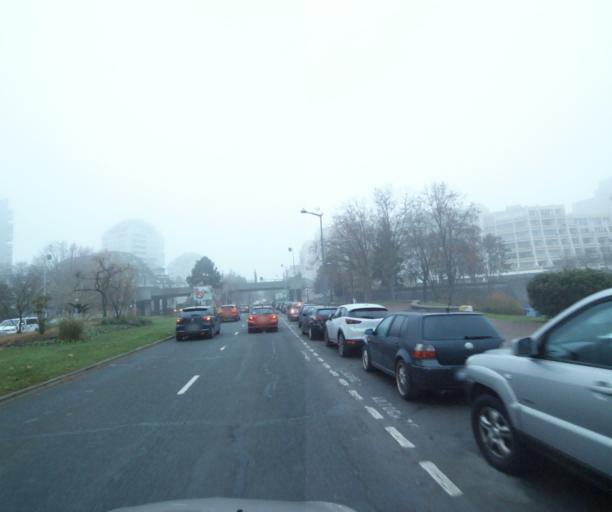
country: FR
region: Ile-de-France
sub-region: Departement du Val-de-Marne
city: Villiers-sur-Marne
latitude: 48.8411
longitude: 2.5503
